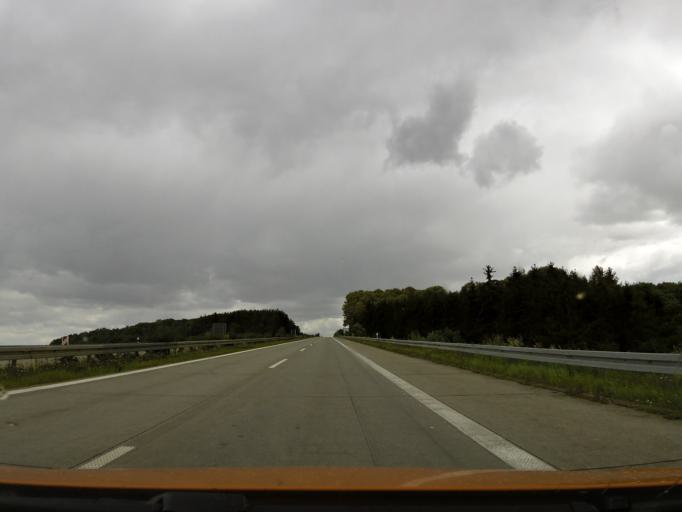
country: DE
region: Brandenburg
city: Brussow
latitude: 53.2948
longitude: 14.1304
